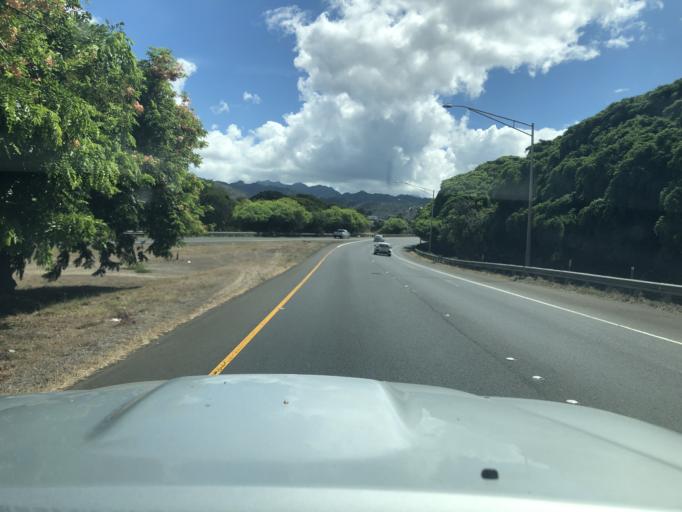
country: US
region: Hawaii
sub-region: Honolulu County
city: Halawa
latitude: 21.3703
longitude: -157.9238
